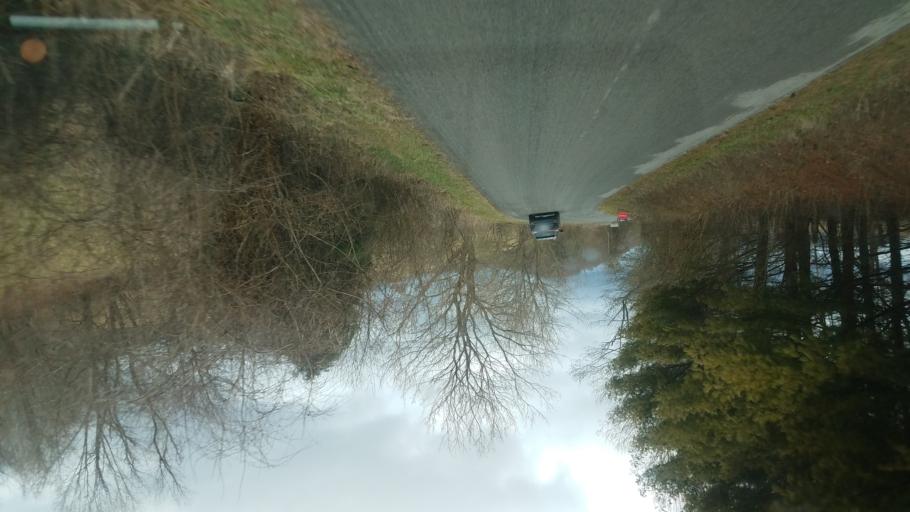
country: US
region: Virginia
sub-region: Giles County
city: Pembroke
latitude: 37.2366
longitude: -80.6842
